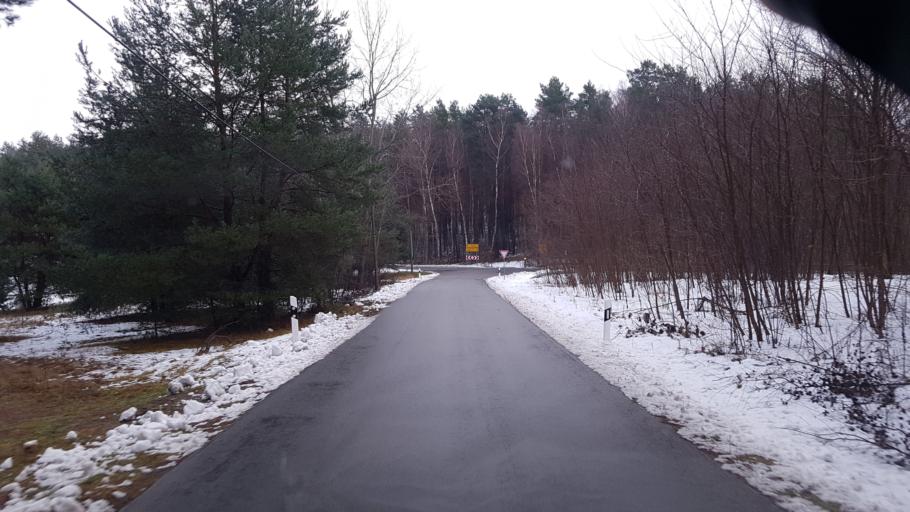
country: DE
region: Brandenburg
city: Lieberose
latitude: 51.9727
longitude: 14.2024
